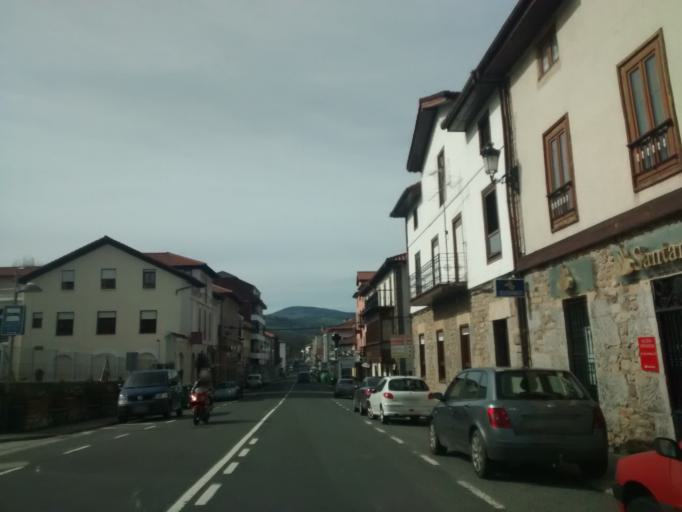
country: ES
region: Cantabria
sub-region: Provincia de Cantabria
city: Santiurde de Toranzo
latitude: 43.1956
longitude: -3.9209
